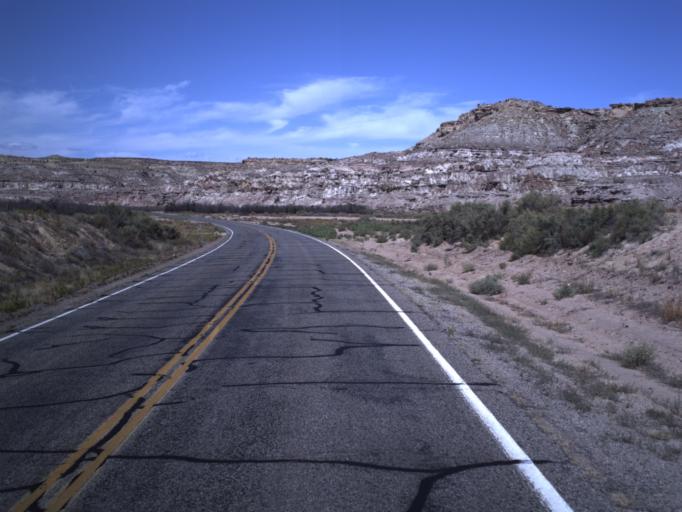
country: US
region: Utah
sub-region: San Juan County
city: Blanding
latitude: 37.2529
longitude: -109.2577
